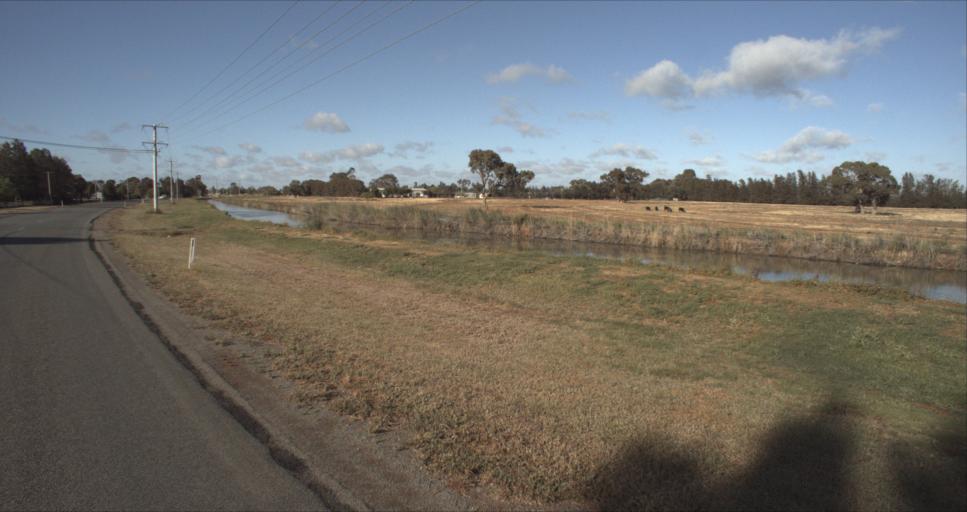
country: AU
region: New South Wales
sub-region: Leeton
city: Leeton
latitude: -34.5348
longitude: 146.3884
